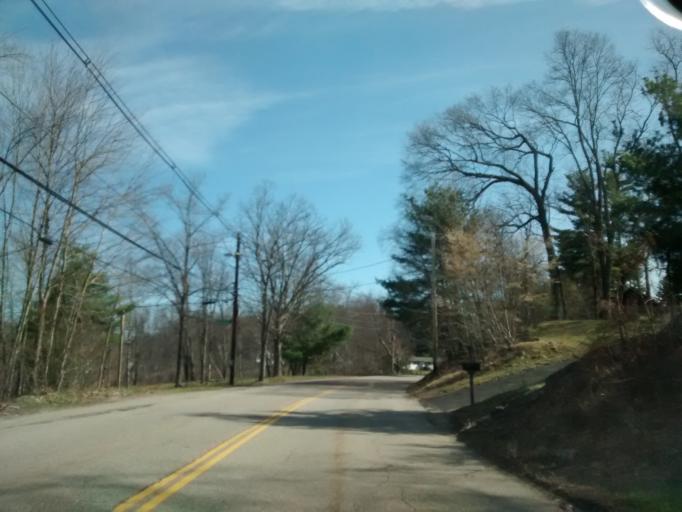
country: US
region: Massachusetts
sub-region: Worcester County
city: Millbury
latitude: 42.2027
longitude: -71.7491
